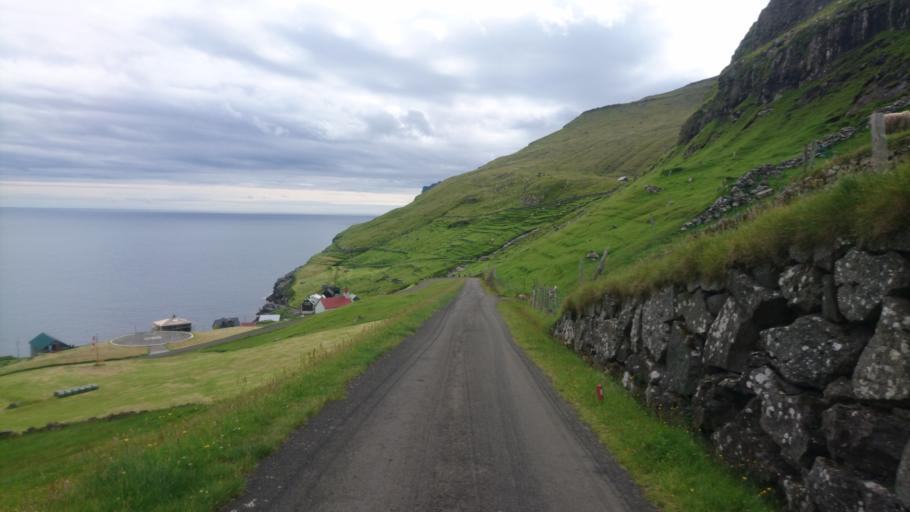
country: FO
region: Nordoyar
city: Klaksvik
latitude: 62.3314
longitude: -6.2775
